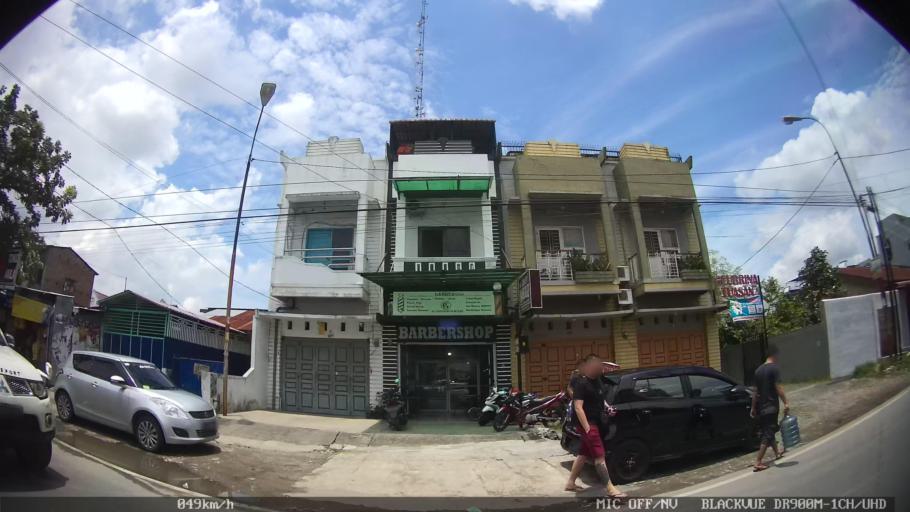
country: ID
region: North Sumatra
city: Medan
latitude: 3.6158
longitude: 98.7013
